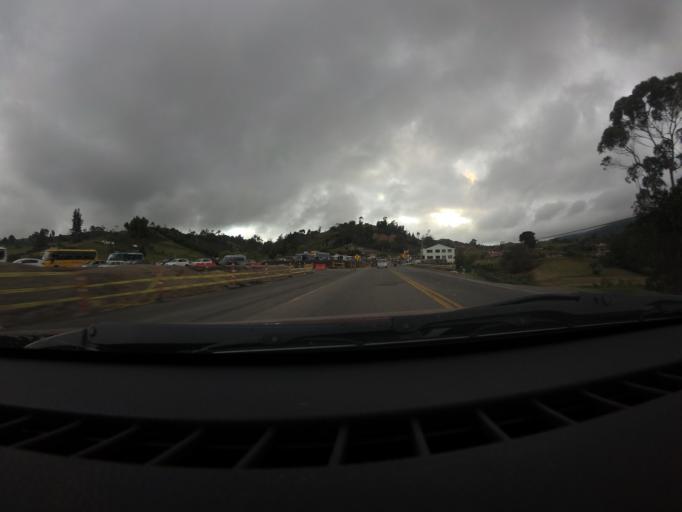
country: CO
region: Boyaca
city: Samaca
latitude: 5.4424
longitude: -73.4375
